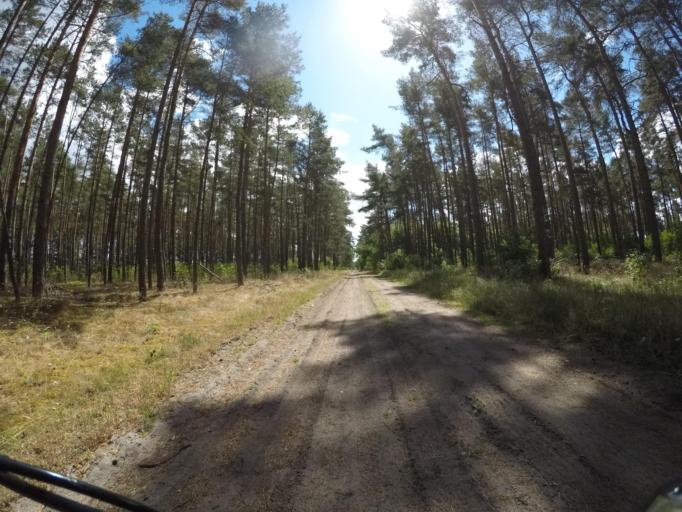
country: DE
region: Lower Saxony
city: Hitzacker
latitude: 53.2127
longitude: 11.0537
